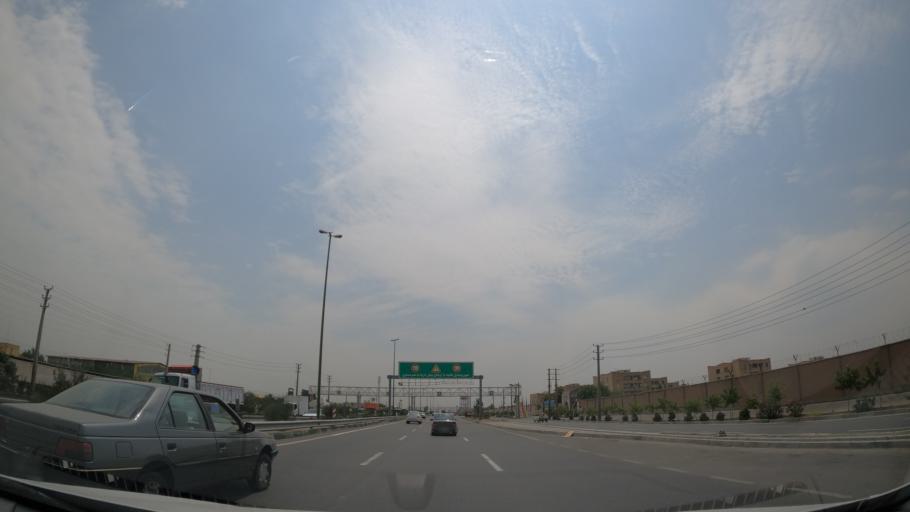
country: IR
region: Tehran
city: Shahr-e Qods
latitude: 35.6973
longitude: 51.1985
